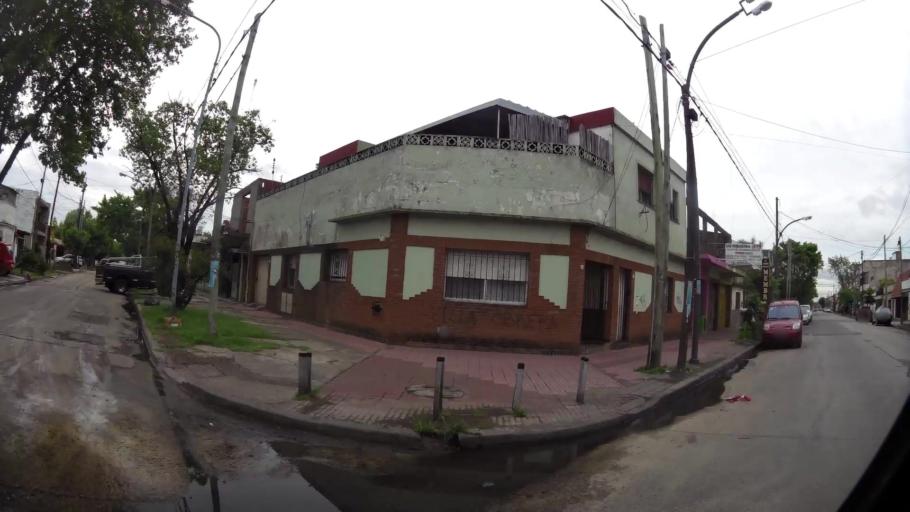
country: AR
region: Buenos Aires
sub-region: Partido de Lanus
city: Lanus
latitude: -34.7202
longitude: -58.3731
